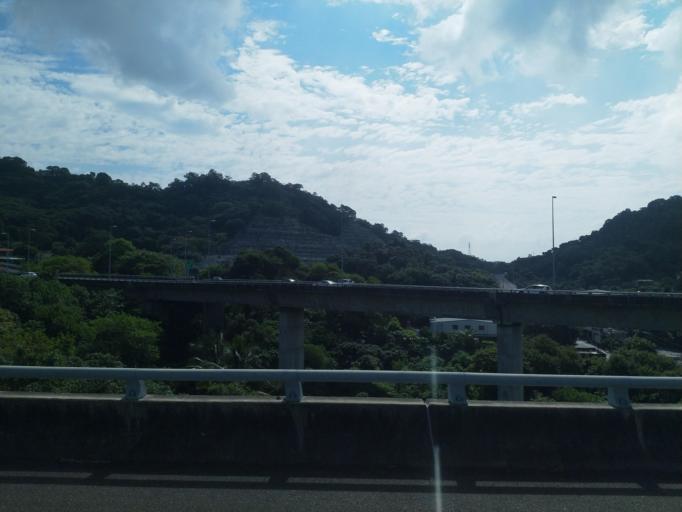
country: TW
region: Taiwan
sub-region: Pingtung
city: Pingtung
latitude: 22.7818
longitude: 120.4245
